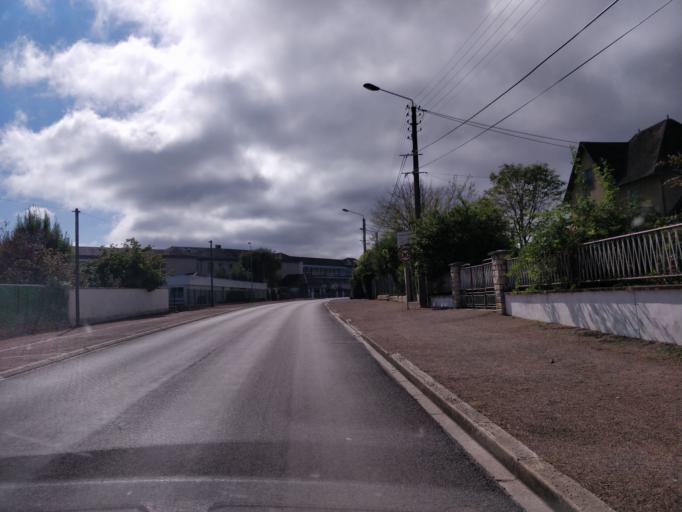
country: FR
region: Bourgogne
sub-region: Departement de l'Yonne
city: Saint-Florentin
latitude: 48.0022
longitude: 3.7265
